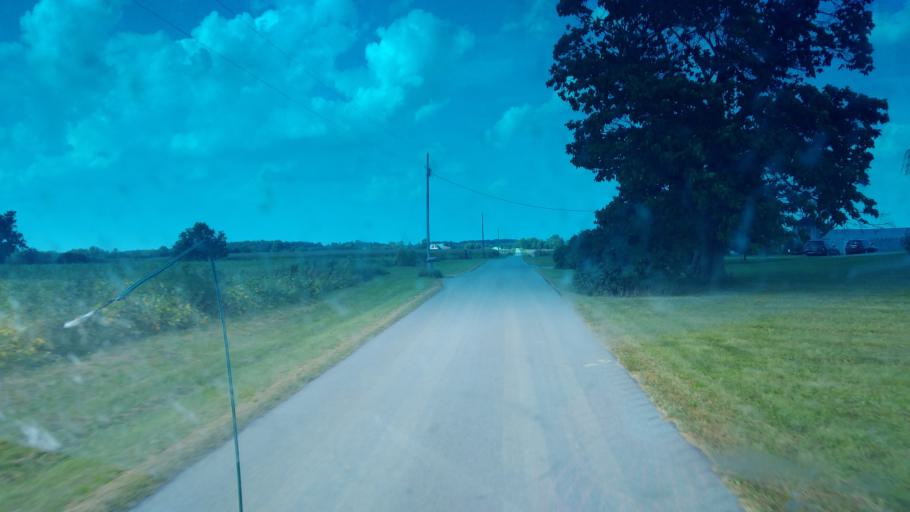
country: US
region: Ohio
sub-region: Hancock County
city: Arlington
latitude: 40.8644
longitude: -83.5855
